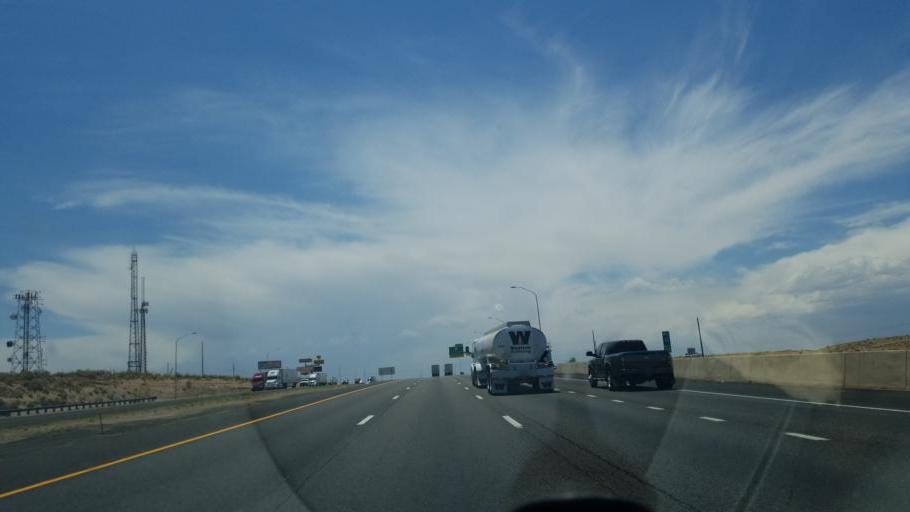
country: US
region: New Mexico
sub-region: Bernalillo County
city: South Valley
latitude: 35.0687
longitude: -106.7809
